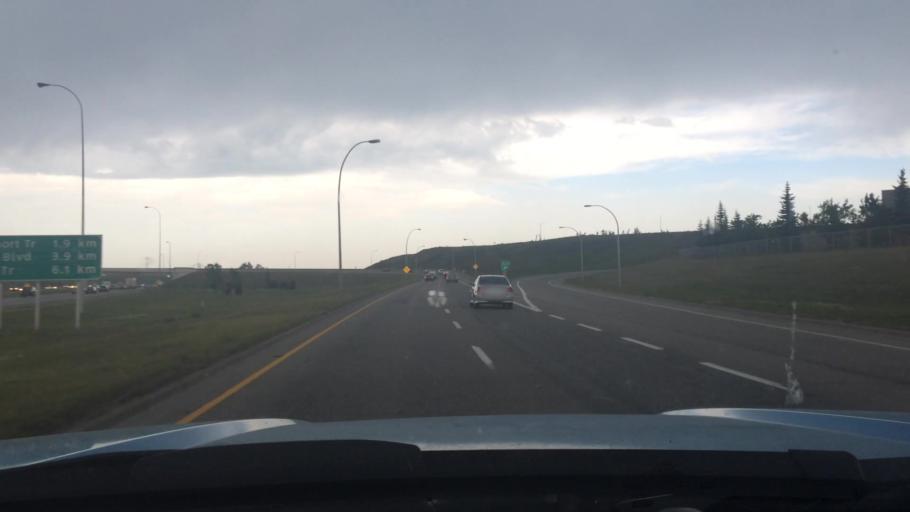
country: CA
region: Alberta
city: Calgary
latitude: 51.1220
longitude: -114.0453
